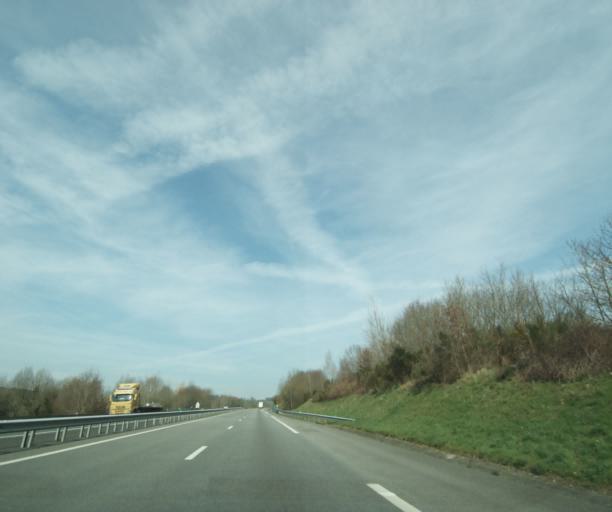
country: FR
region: Limousin
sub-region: Departement de la Correze
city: Vigeois
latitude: 45.4249
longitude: 1.5153
